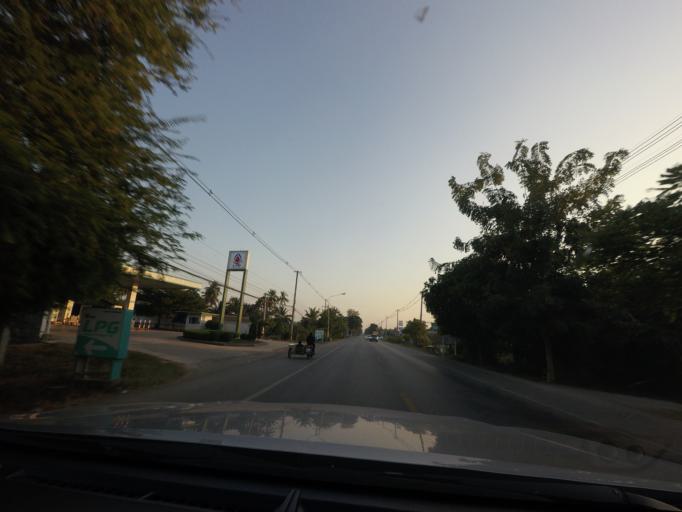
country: TH
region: Sukhothai
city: Si Samrong
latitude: 17.1323
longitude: 99.8502
